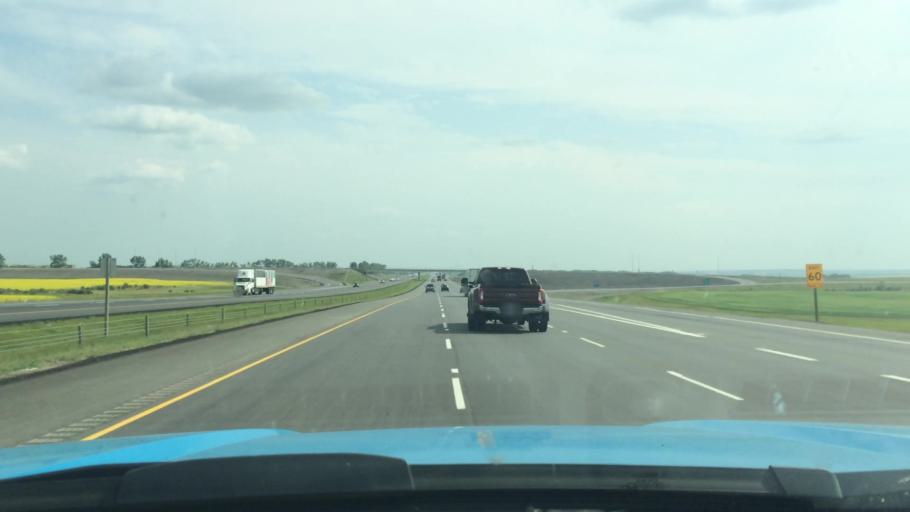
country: CA
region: Alberta
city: Crossfield
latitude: 51.3927
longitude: -114.0020
